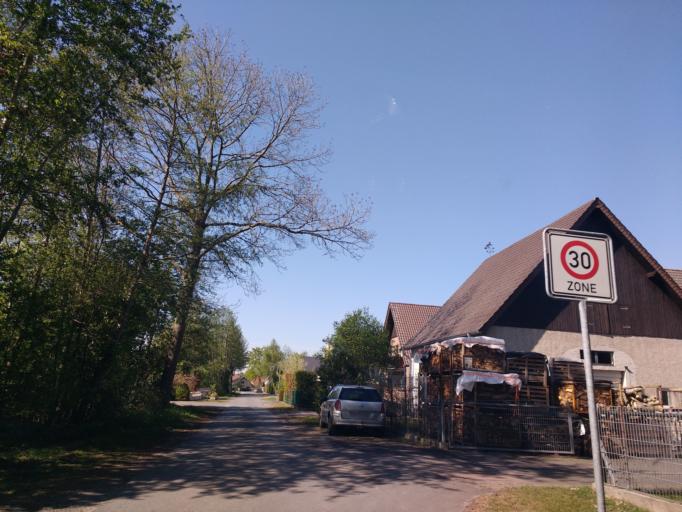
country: DE
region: North Rhine-Westphalia
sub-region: Regierungsbezirk Detmold
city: Delbruck
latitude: 51.7552
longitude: 8.5695
